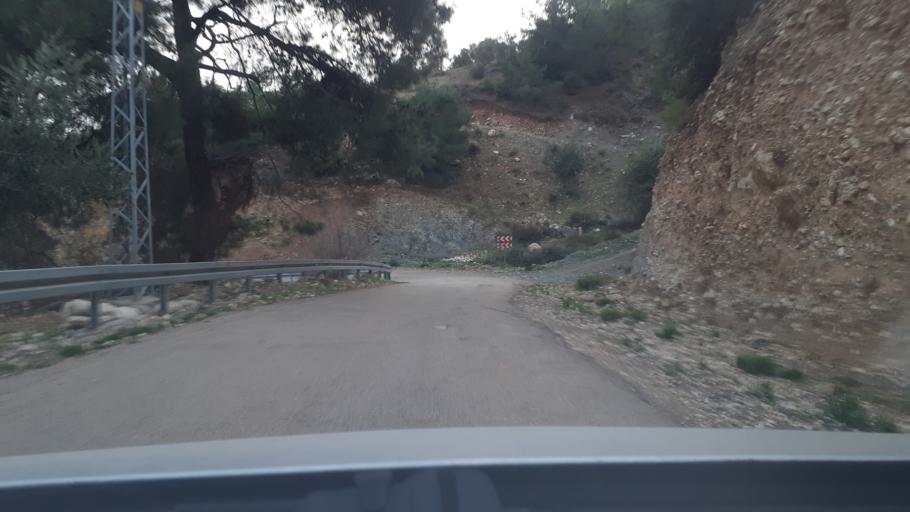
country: TR
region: Hatay
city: Kirikhan
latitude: 36.5311
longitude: 36.3157
